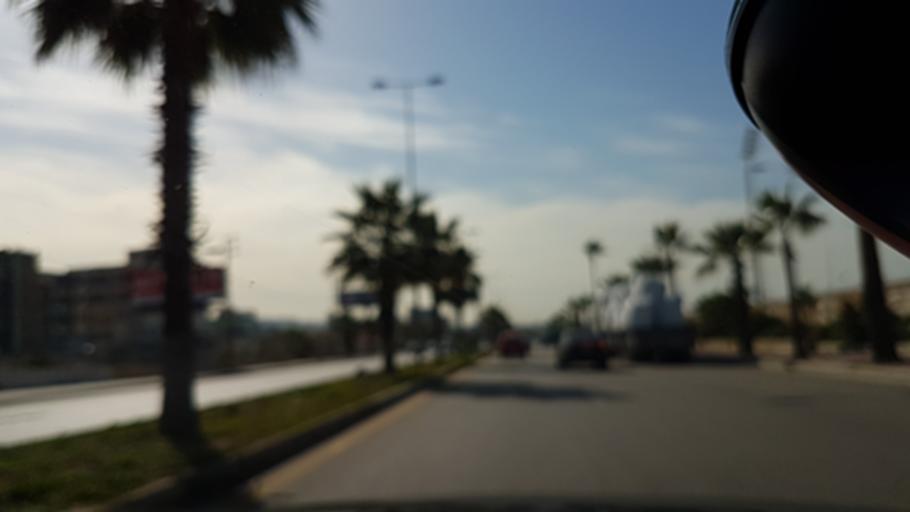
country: LB
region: Liban-Sud
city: Sidon
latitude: 33.5863
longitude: 35.3863
